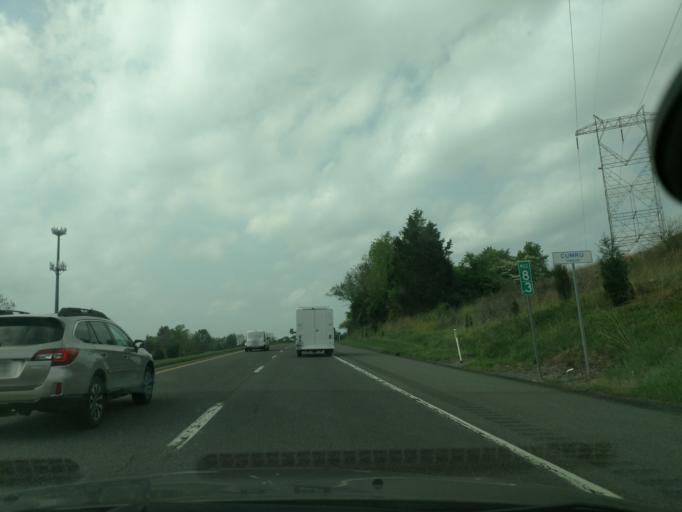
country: US
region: Pennsylvania
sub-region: Berks County
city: Flying Hills
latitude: 40.2657
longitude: -75.9157
